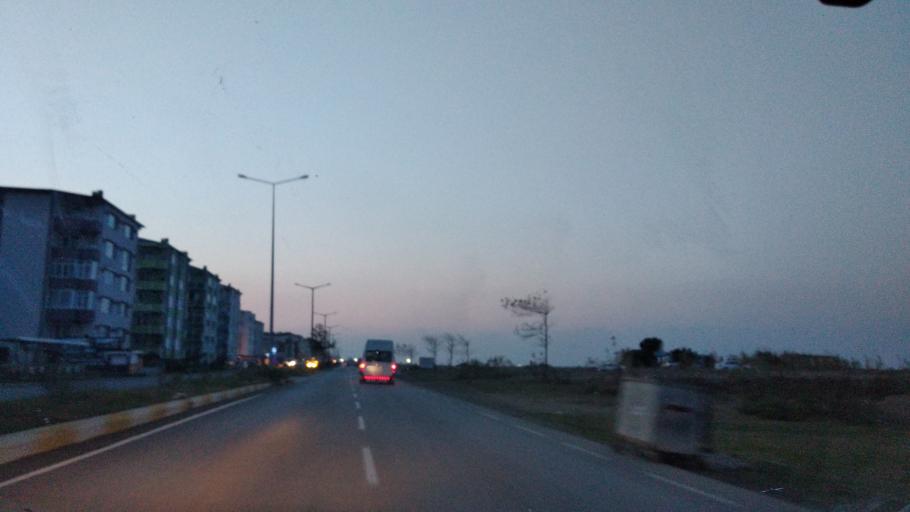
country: TR
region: Sakarya
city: Karasu
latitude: 41.0997
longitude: 30.7213
